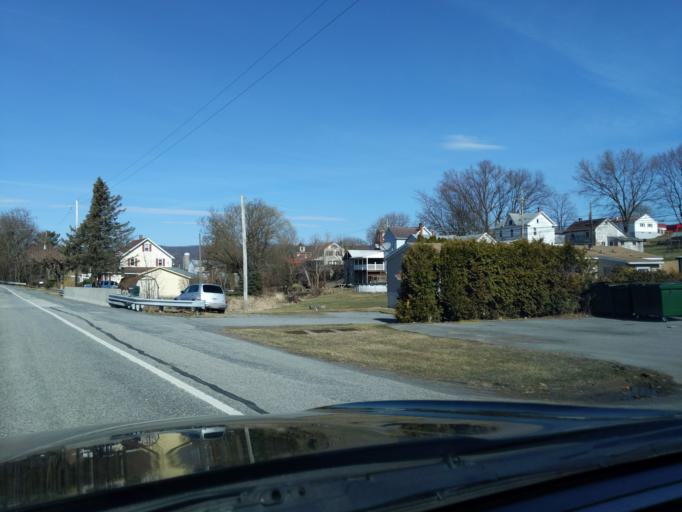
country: US
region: Pennsylvania
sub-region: Blair County
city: Roaring Spring
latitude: 40.3340
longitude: -78.3721
